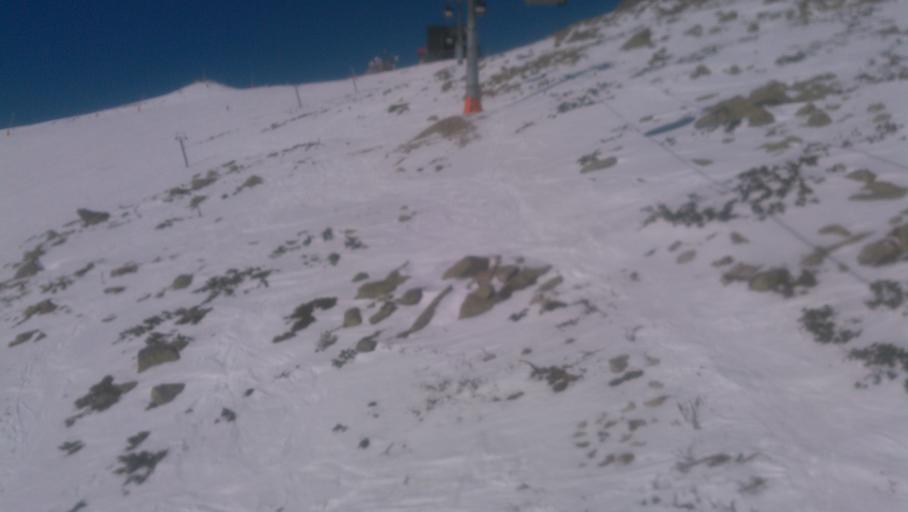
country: SK
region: Banskobystricky
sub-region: Okres Banska Bystrica
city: Brezno
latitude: 48.9404
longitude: 19.5927
